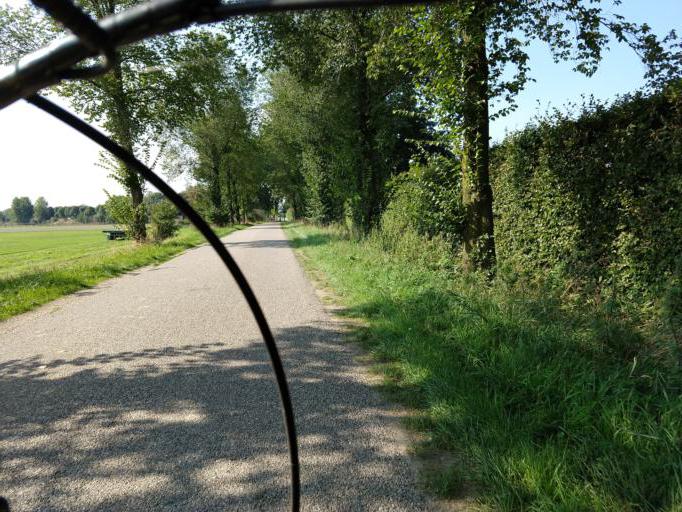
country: NL
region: Zeeland
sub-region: Gemeente Goes
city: Goes
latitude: 51.4371
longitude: 3.8346
